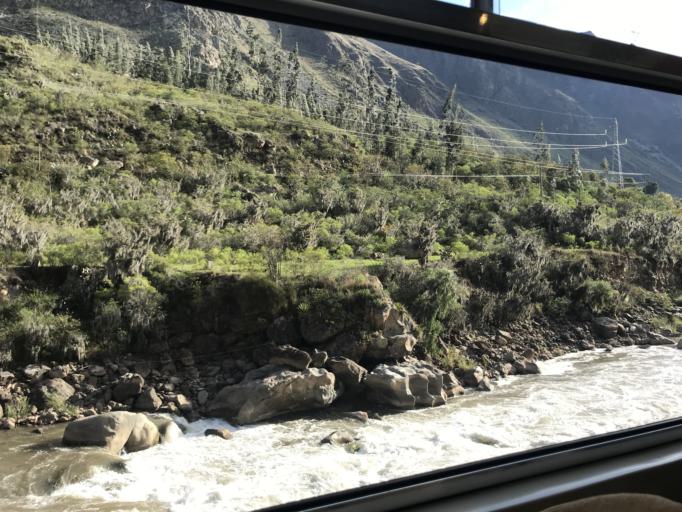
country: PE
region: Cusco
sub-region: Provincia de Urubamba
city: Ollantaytambo
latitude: -13.2264
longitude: -72.4001
